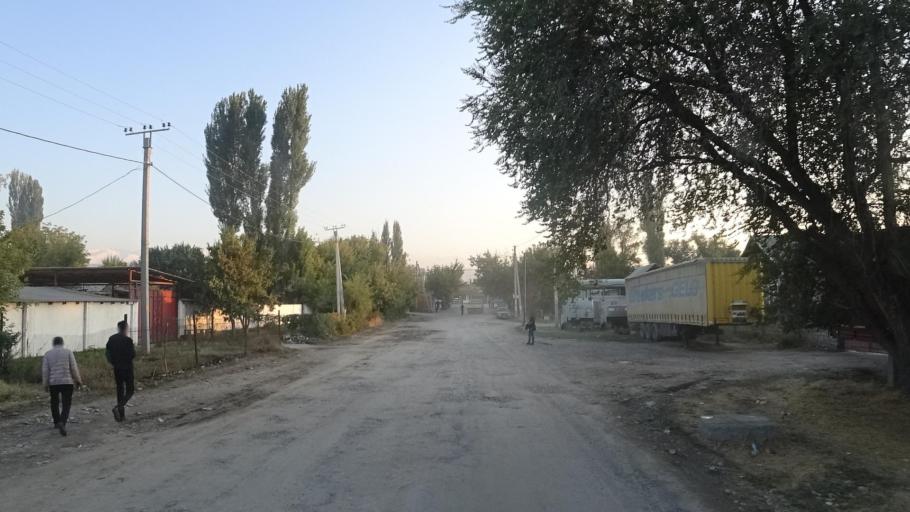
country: KG
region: Chuy
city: Lebedinovka
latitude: 42.8758
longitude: 74.7189
